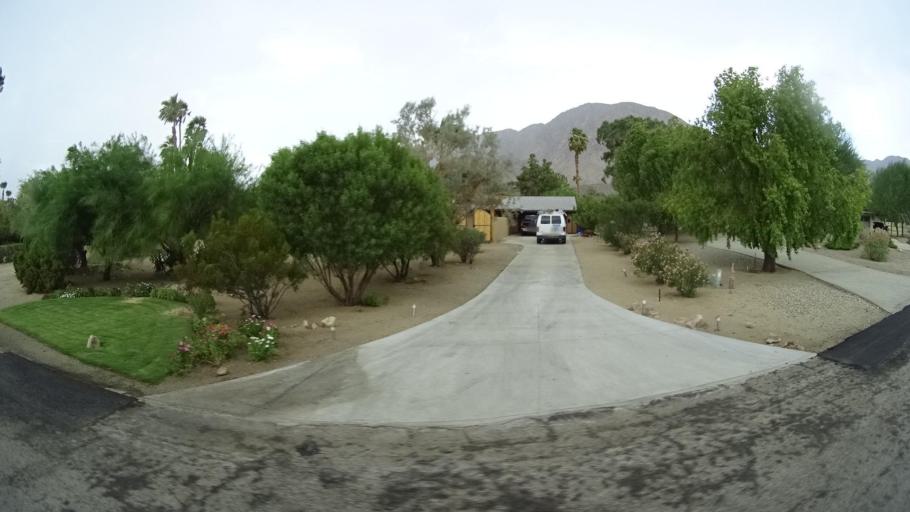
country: US
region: California
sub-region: San Diego County
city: Borrego Springs
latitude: 33.2950
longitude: -116.3881
